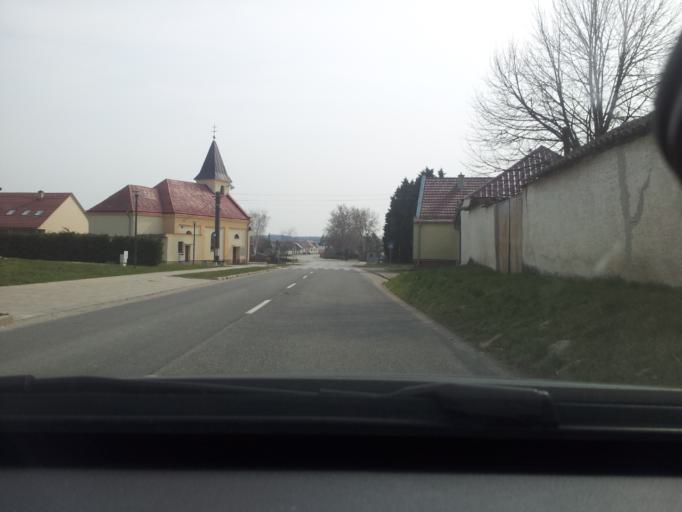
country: SK
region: Trnavsky
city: Leopoldov
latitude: 48.4593
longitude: 17.7145
